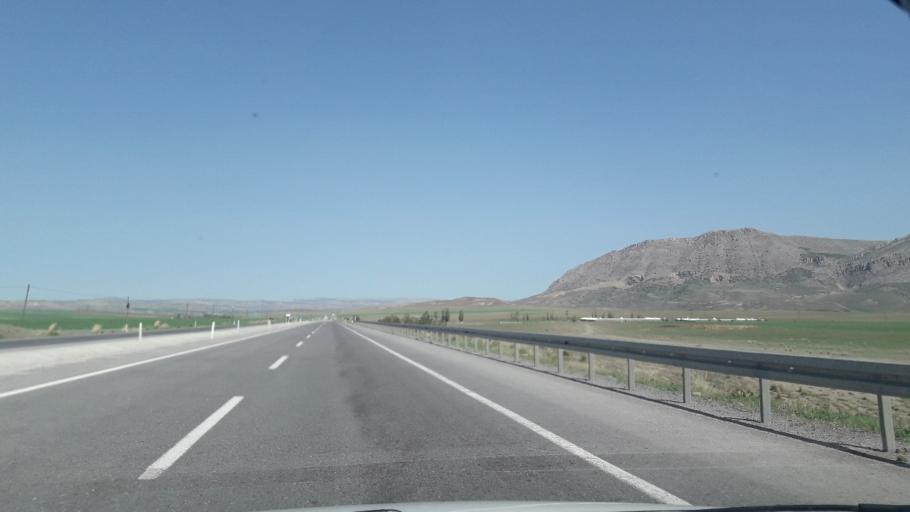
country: TR
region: Sivas
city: Deliktas
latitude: 39.3668
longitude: 37.1220
